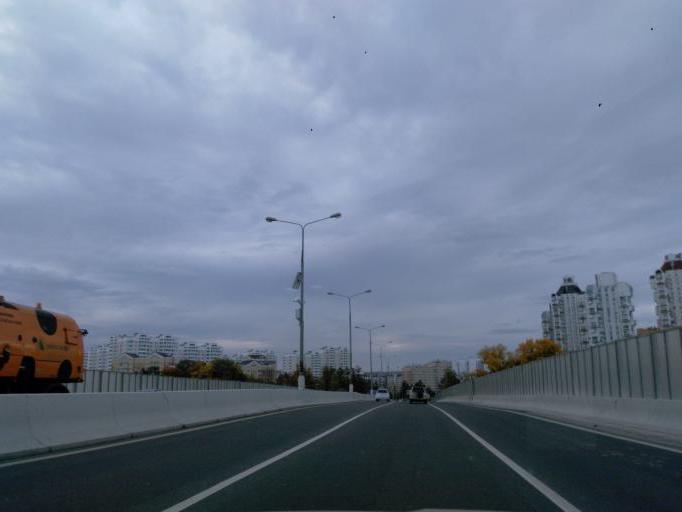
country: RU
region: Moscow
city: Zelenograd
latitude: 55.9800
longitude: 37.1721
